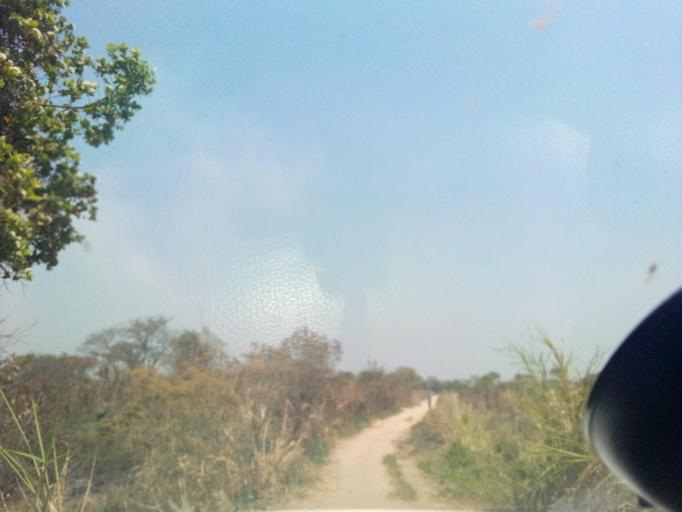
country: ZM
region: Copperbelt
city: Kataba
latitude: -12.2450
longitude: 30.3308
